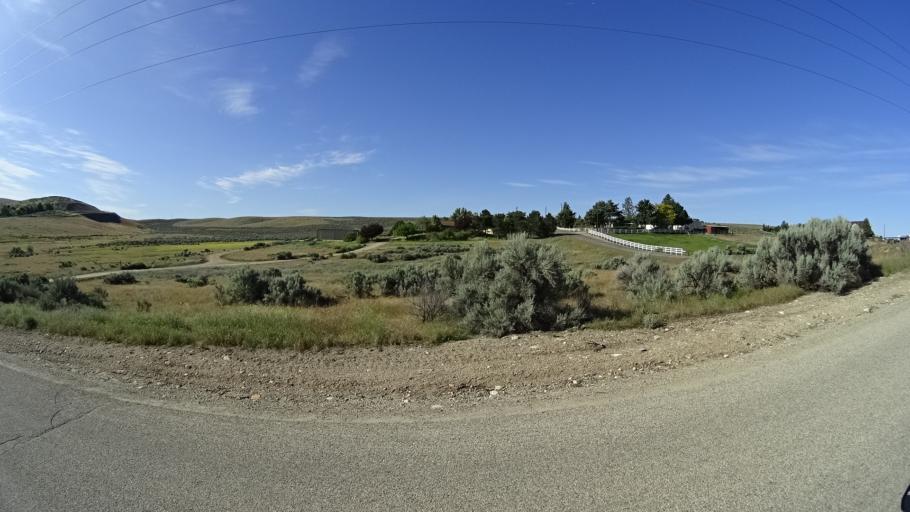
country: US
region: Idaho
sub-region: Ada County
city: Garden City
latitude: 43.5247
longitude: -116.2802
